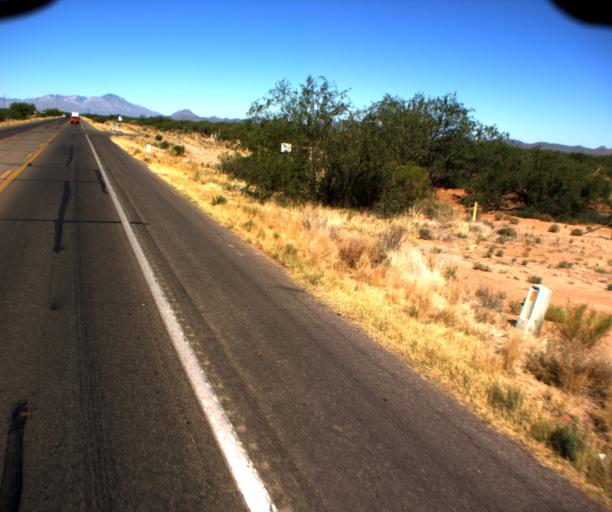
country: US
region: Arizona
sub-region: Pima County
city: Three Points
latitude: 32.1112
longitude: -111.2272
